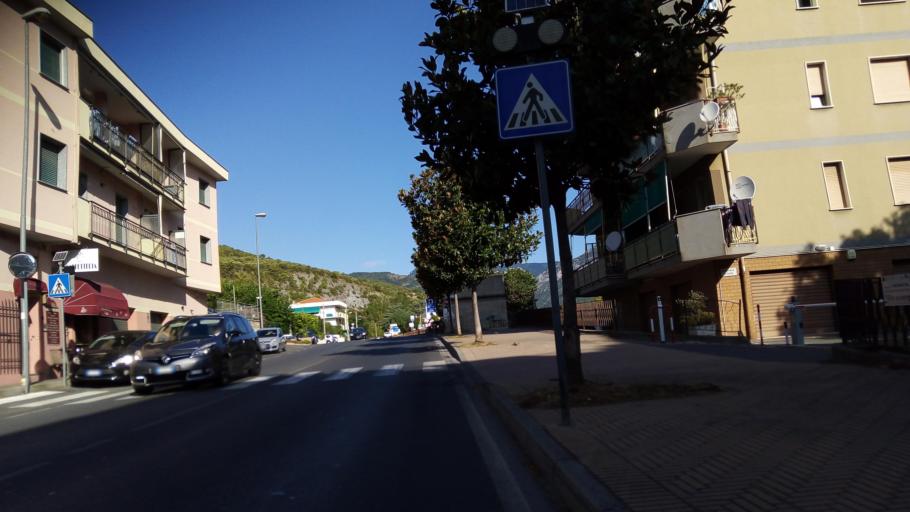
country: IT
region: Liguria
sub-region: Provincia di Savona
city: Borghetto Santo Spirito
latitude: 44.1135
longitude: 8.2333
